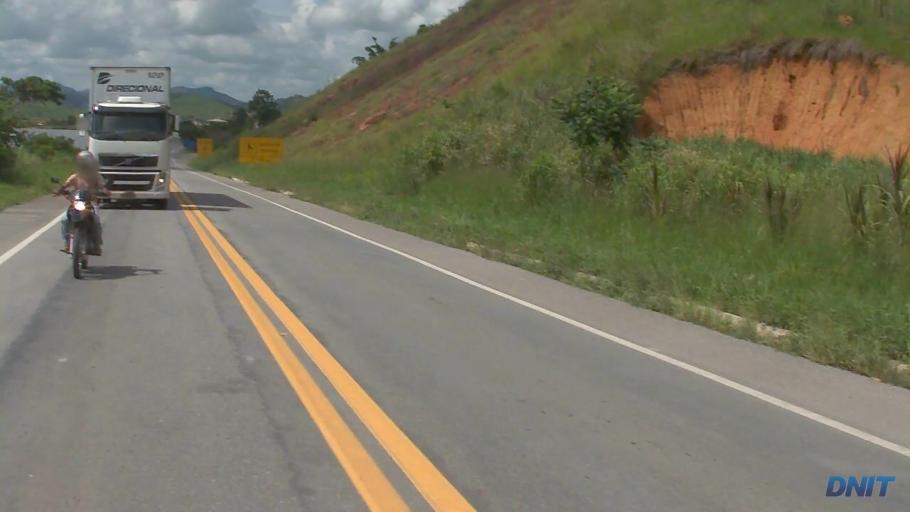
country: BR
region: Minas Gerais
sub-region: Governador Valadares
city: Governador Valadares
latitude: -19.0444
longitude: -42.1520
